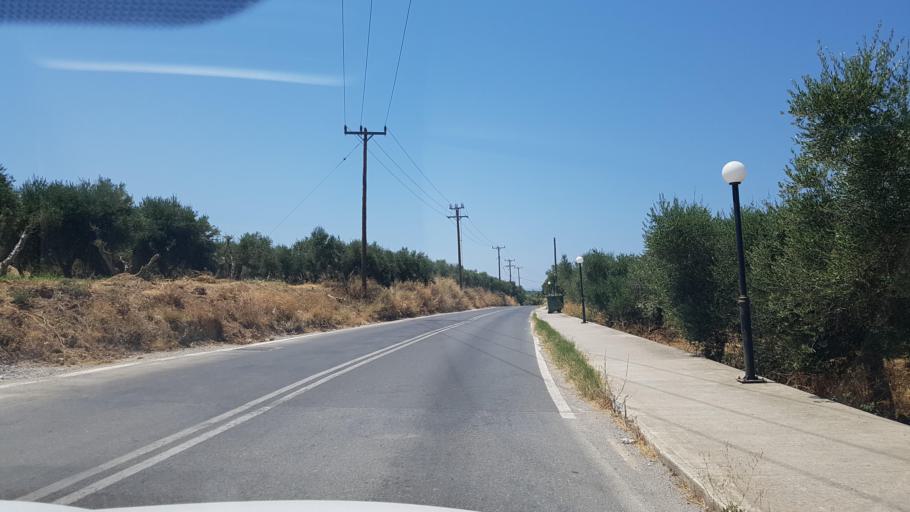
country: GR
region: Crete
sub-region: Nomos Rethymnis
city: Rethymno
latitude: 35.3576
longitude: 24.5784
